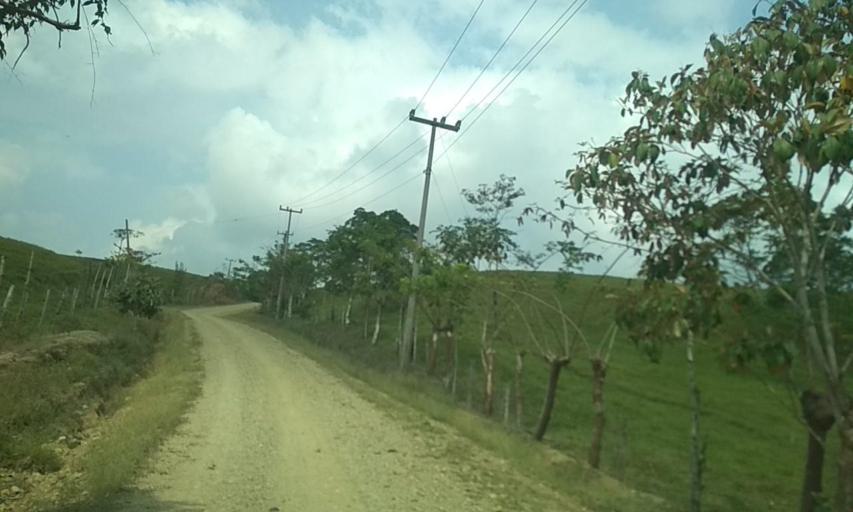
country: MX
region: Tabasco
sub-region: Huimanguillo
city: Francisco Rueda
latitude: 17.6570
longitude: -93.7559
